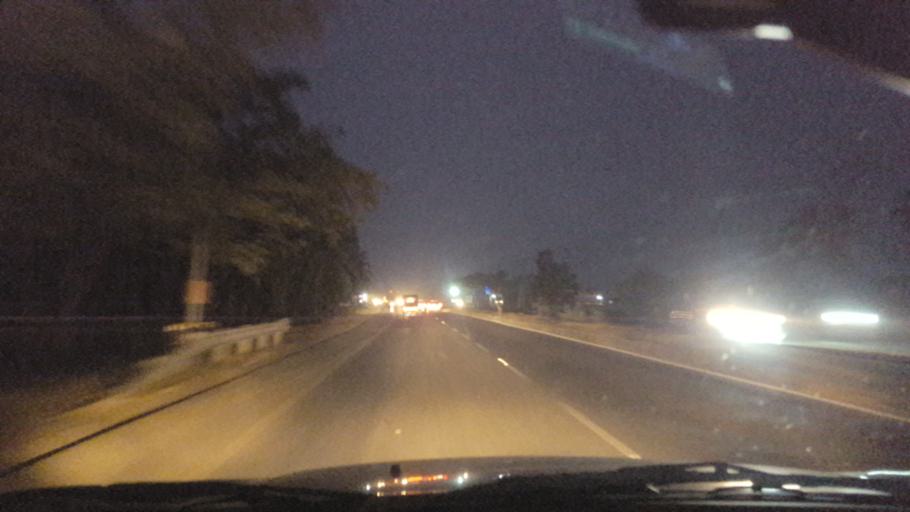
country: IN
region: Andhra Pradesh
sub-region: East Godavari
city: Peddapuram
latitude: 17.1374
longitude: 81.9687
